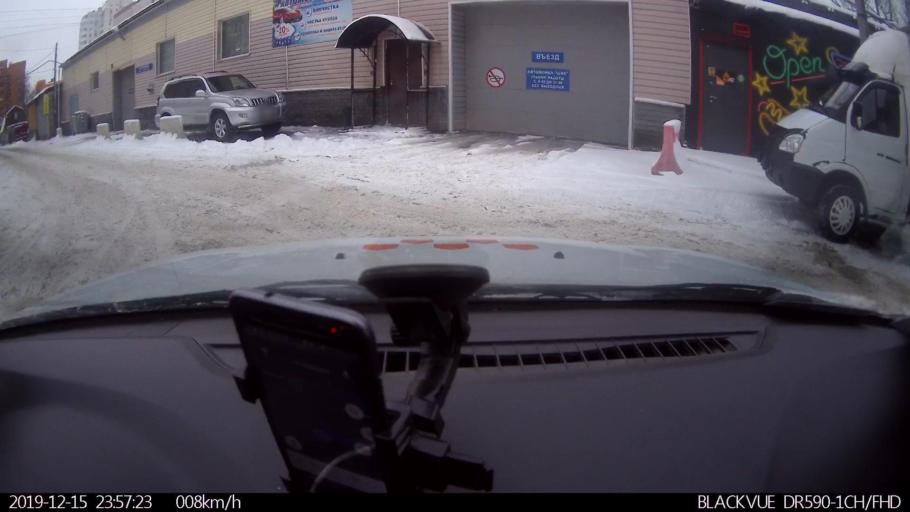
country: RU
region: Nizjnij Novgorod
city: Nizhniy Novgorod
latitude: 56.3056
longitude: 43.9973
